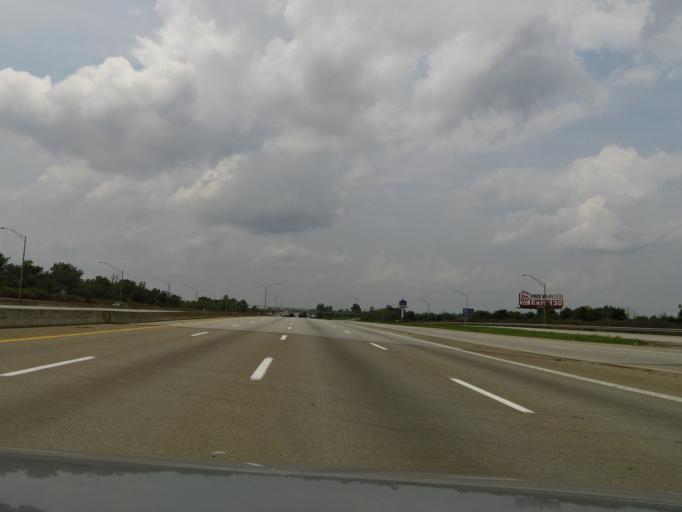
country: US
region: Kentucky
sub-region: Jefferson County
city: Okolona
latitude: 38.1519
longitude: -85.7142
